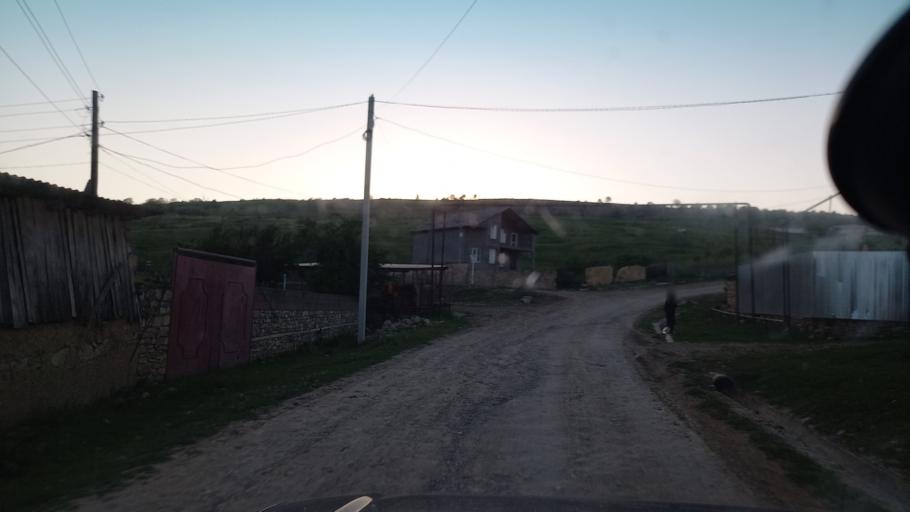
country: RU
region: Dagestan
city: Khuchni
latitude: 42.0321
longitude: 47.9685
